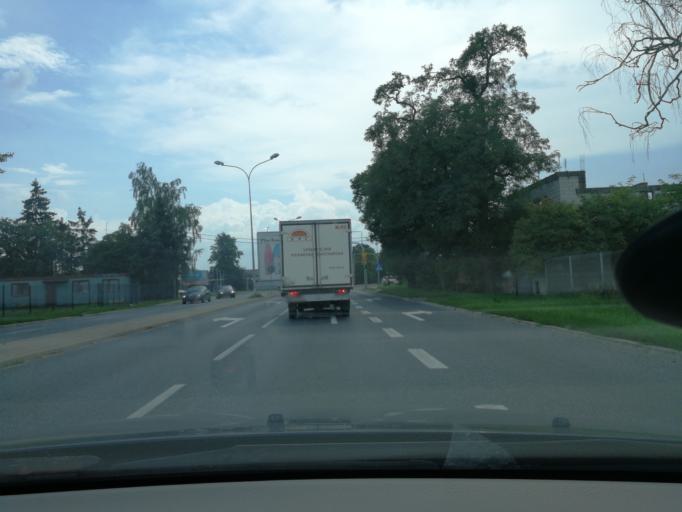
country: PL
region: Masovian Voivodeship
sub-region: Powiat pruszkowski
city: Piastow
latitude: 52.2152
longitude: 20.8388
